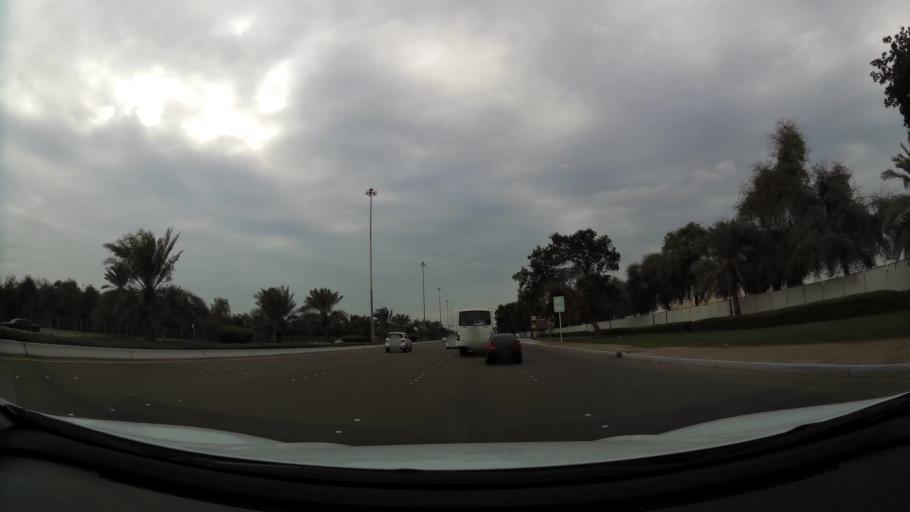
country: AE
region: Abu Dhabi
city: Abu Dhabi
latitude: 24.4298
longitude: 54.3918
